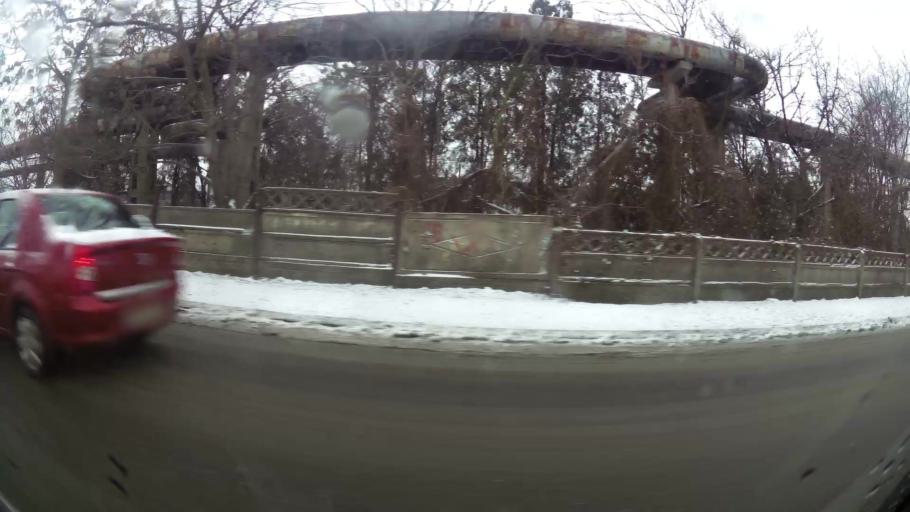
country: RO
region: Prahova
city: Ploiesti
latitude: 44.9224
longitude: 26.0145
